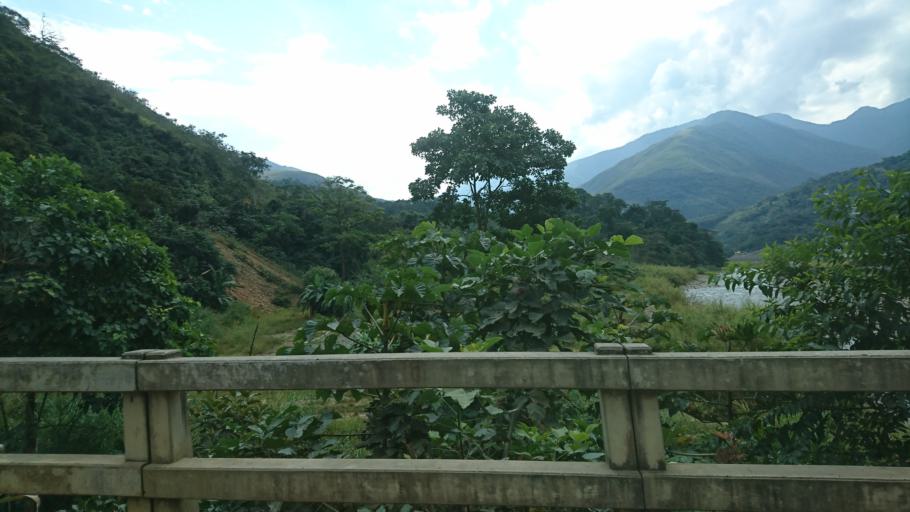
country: BO
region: La Paz
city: Coroico
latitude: -16.1676
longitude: -67.7296
